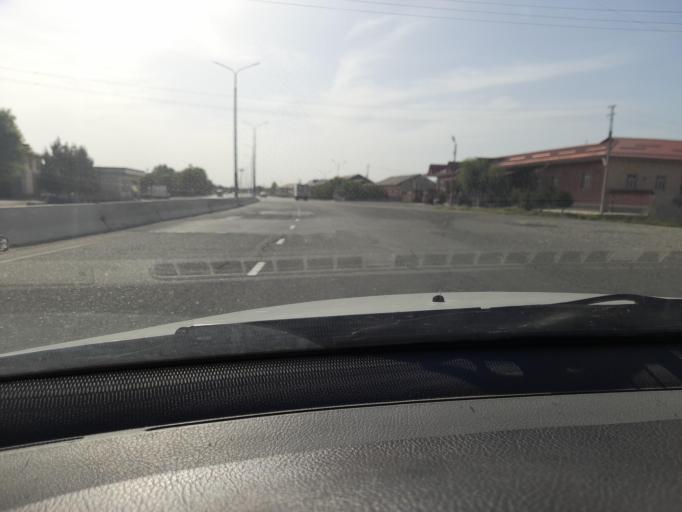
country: UZ
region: Samarqand
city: Kattaqo'rg'on
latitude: 39.9230
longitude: 66.2846
